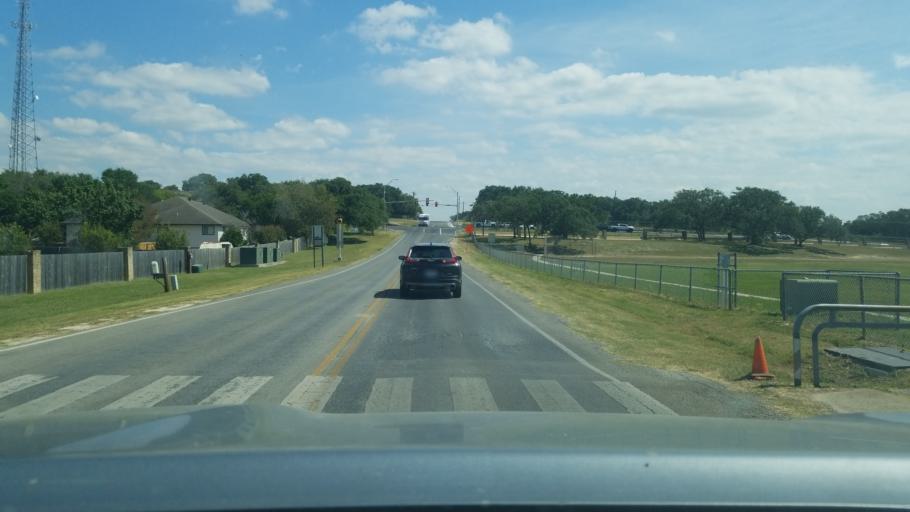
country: US
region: Texas
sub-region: Bexar County
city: Fair Oaks Ranch
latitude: 29.7310
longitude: -98.6253
